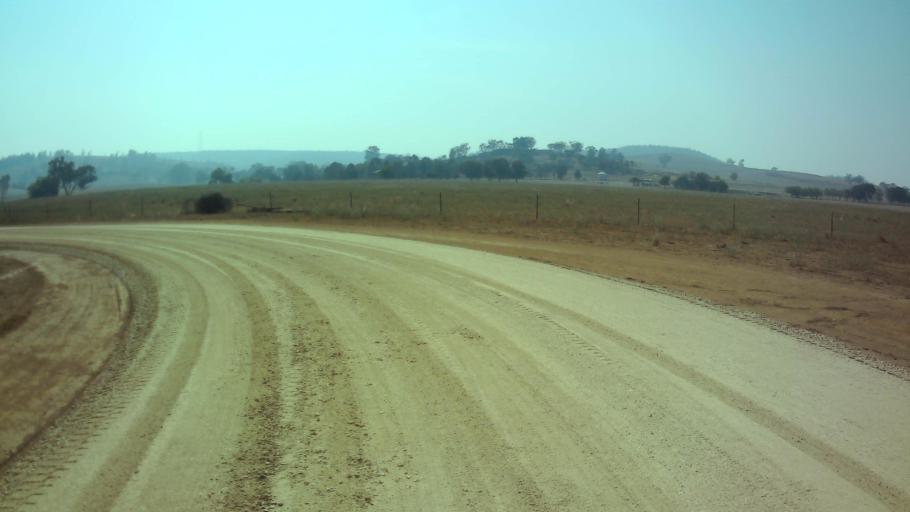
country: AU
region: New South Wales
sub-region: Weddin
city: Grenfell
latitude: -33.8582
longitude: 148.1107
